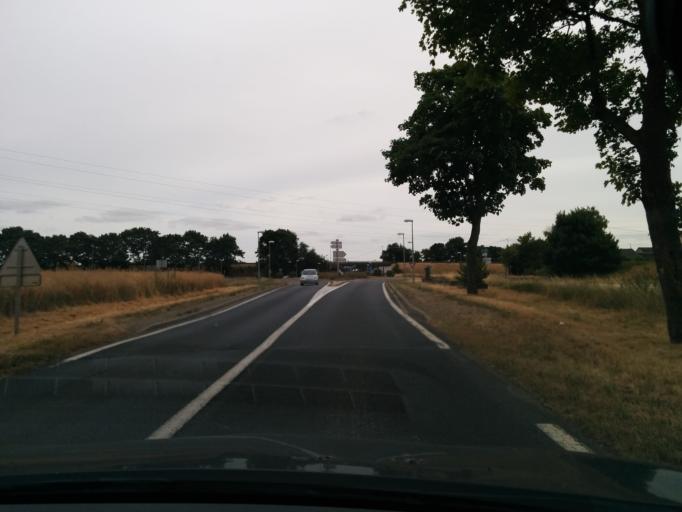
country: FR
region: Ile-de-France
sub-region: Departement de l'Essonne
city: Angerville
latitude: 48.3193
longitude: 1.9961
